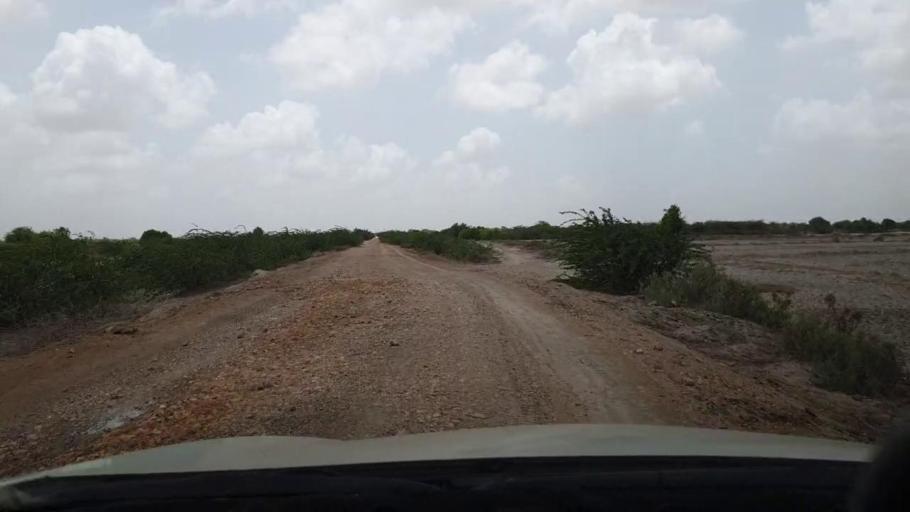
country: PK
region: Sindh
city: Kadhan
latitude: 24.3726
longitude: 68.9276
